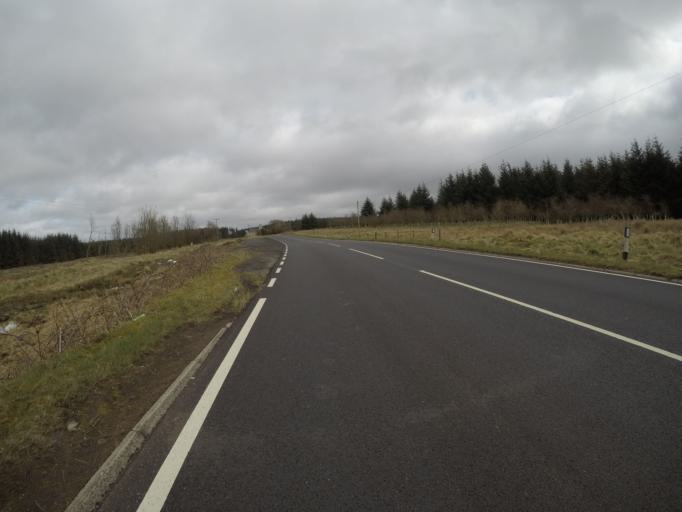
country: GB
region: Scotland
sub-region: East Renfrewshire
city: Newton Mearns
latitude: 55.7020
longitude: -4.3782
